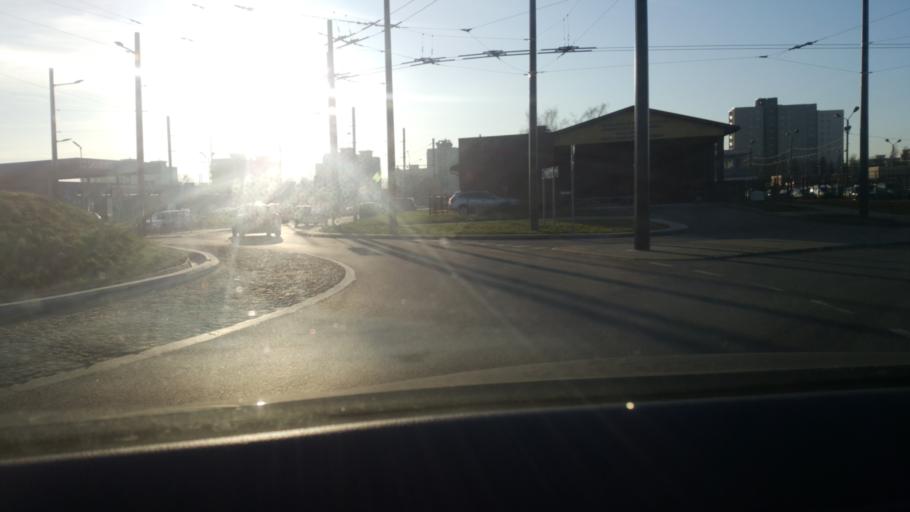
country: LT
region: Kauno apskritis
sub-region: Kaunas
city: Eiguliai
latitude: 54.9340
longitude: 23.9426
